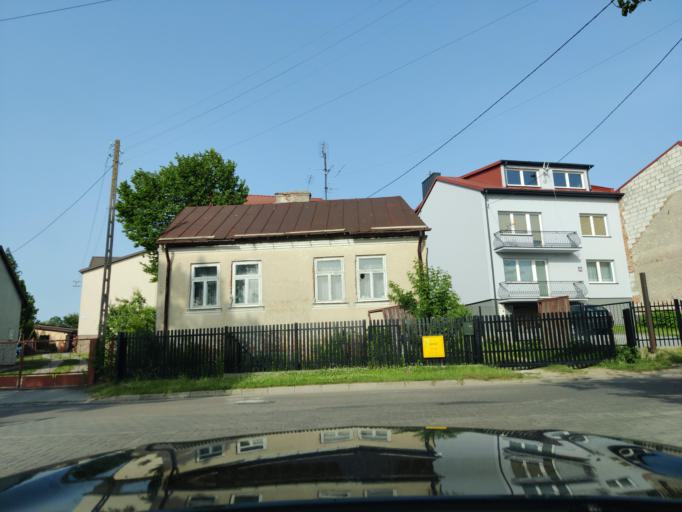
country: PL
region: Masovian Voivodeship
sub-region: Powiat wyszkowski
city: Wyszkow
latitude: 52.5967
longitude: 21.4586
